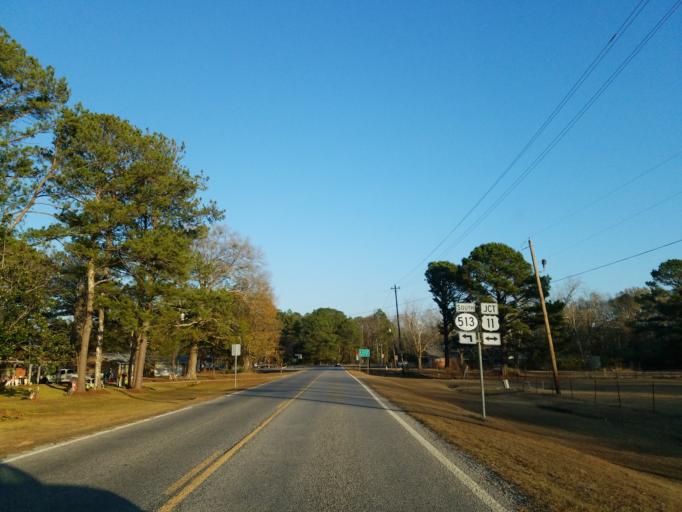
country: US
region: Mississippi
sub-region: Clarke County
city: Stonewall
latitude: 32.1704
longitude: -88.8345
